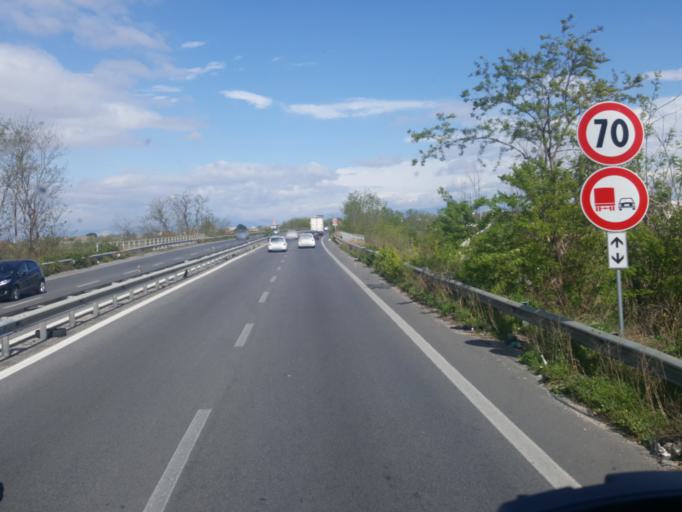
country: IT
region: Campania
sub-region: Provincia di Napoli
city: Qualiano
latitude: 40.9354
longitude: 14.1452
